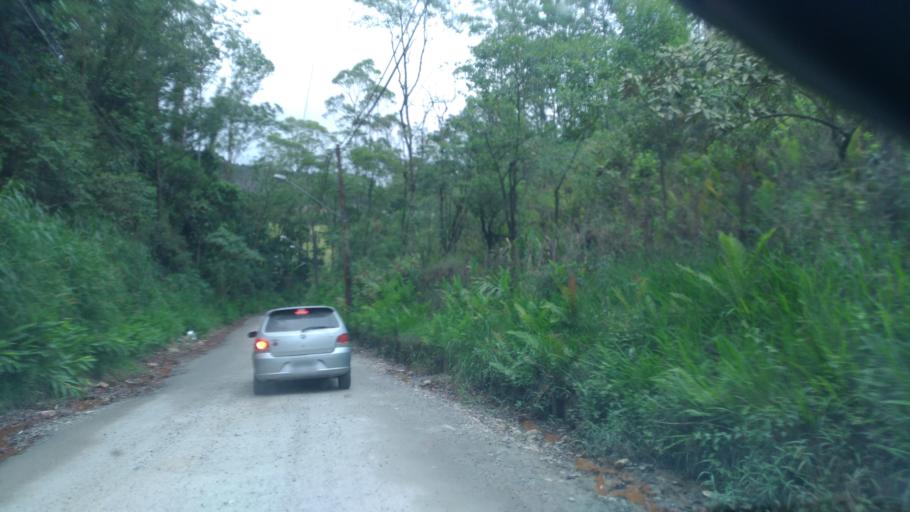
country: BR
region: Sao Paulo
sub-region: Sao Bernardo Do Campo
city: Sao Bernardo do Campo
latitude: -23.7393
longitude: -46.5198
